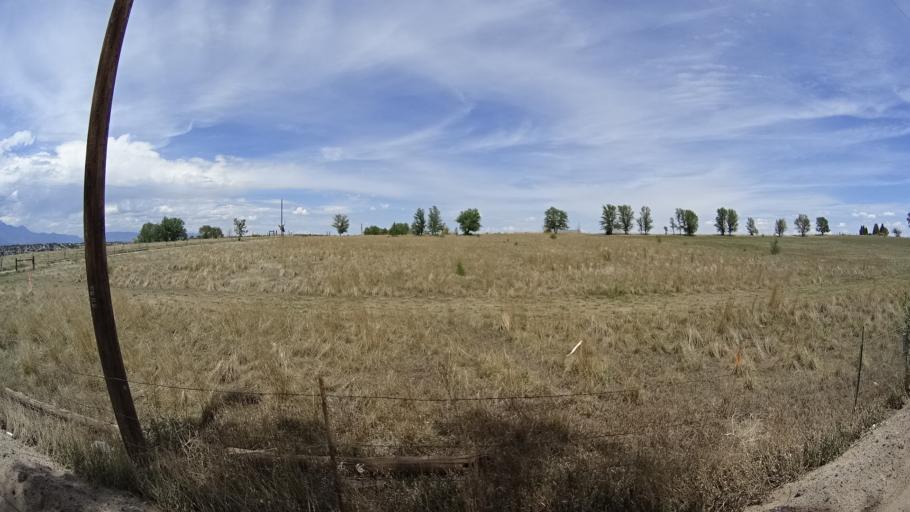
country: US
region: Colorado
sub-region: El Paso County
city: Fountain
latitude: 38.6940
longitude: -104.6710
